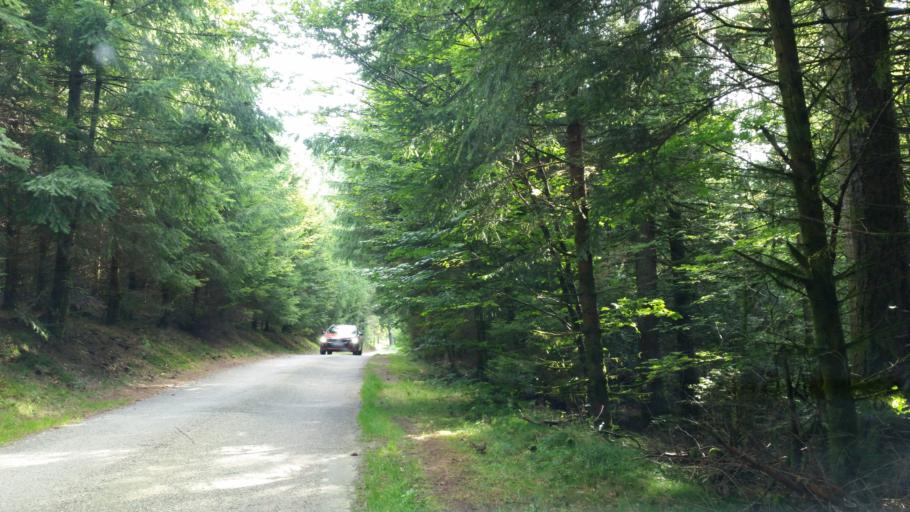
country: FR
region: Lorraine
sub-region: Departement des Vosges
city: Vecoux
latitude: 47.9649
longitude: 6.5878
